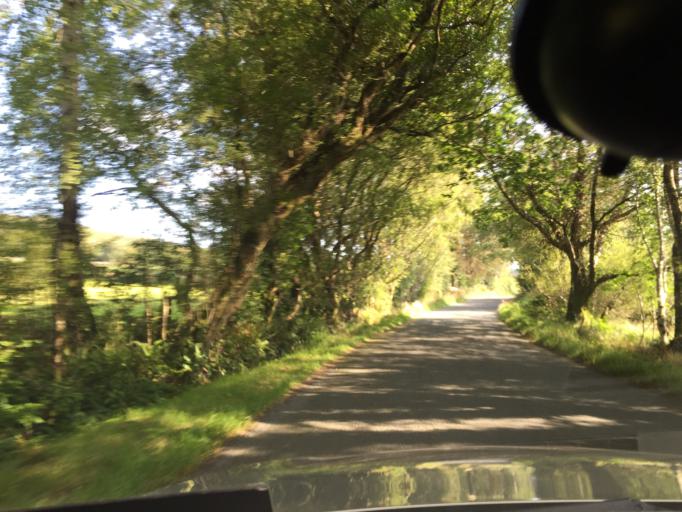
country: IE
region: Leinster
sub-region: Wicklow
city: Rathdrum
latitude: 53.0225
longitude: -6.3071
